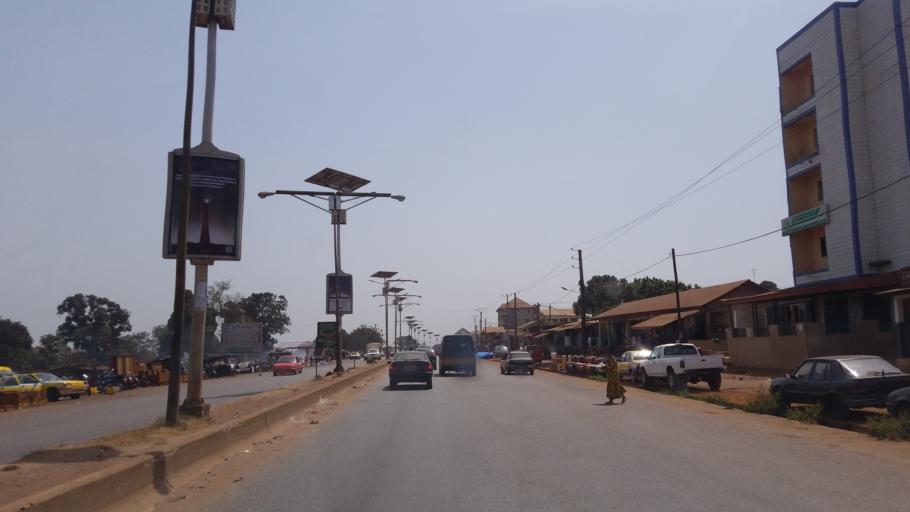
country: GN
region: Conakry
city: Conakry
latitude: 9.6141
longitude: -13.6074
